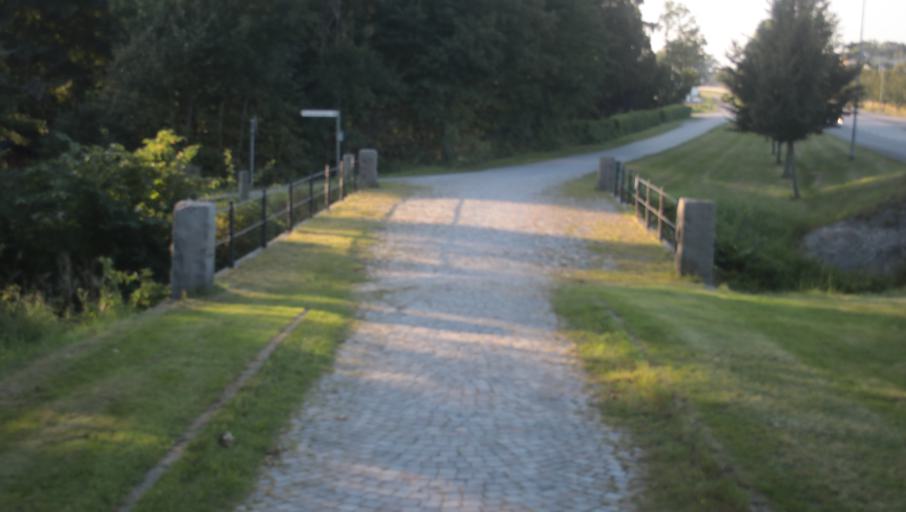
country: SE
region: Blekinge
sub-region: Karlshamns Kommun
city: Karlshamn
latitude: 56.1907
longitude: 14.8447
